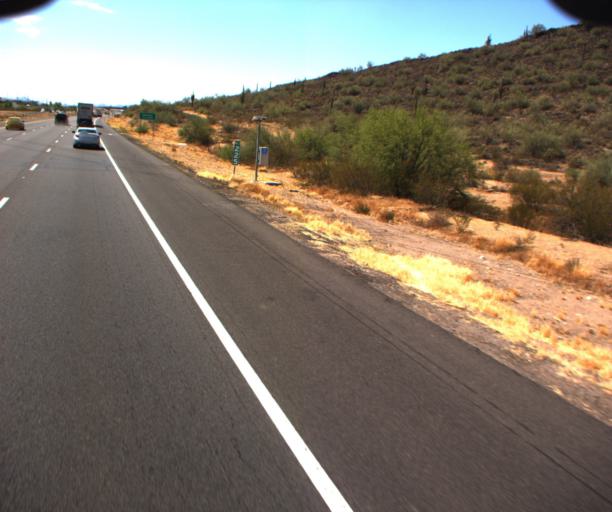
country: US
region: Arizona
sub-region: Maricopa County
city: Anthem
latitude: 33.8129
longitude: -112.1391
